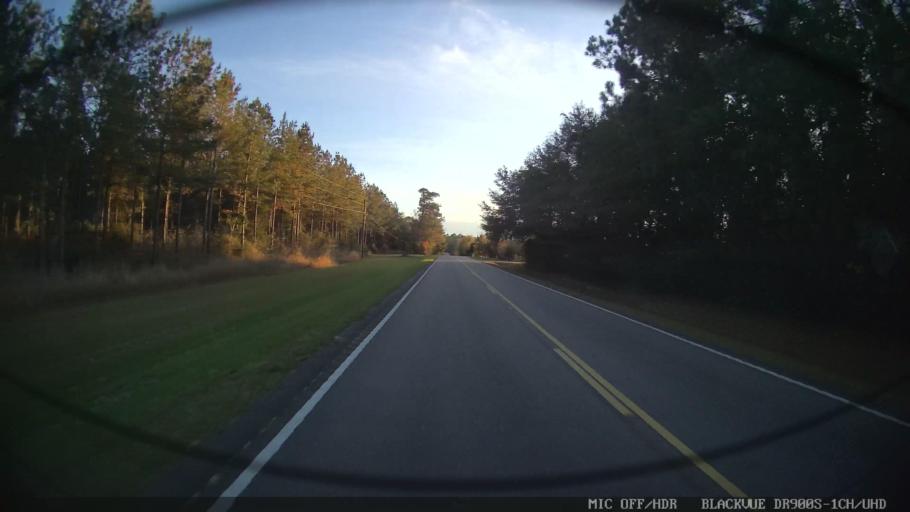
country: US
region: Mississippi
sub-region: Stone County
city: Wiggins
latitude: 31.0148
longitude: -89.2554
